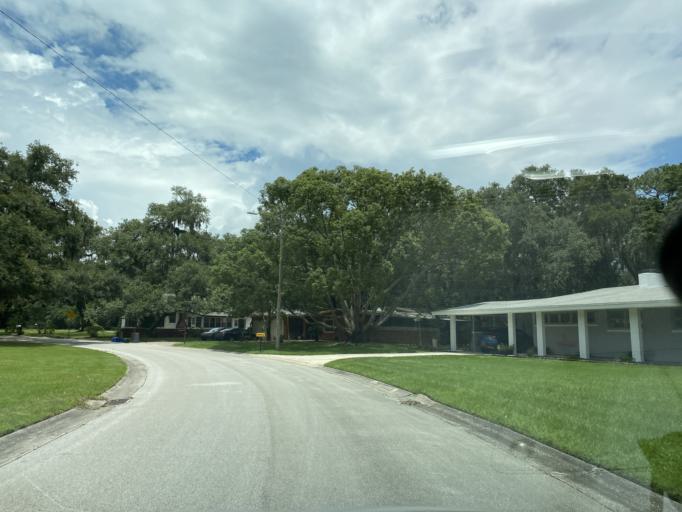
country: US
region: Florida
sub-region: Seminole County
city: Sanford
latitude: 28.7914
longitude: -81.2555
